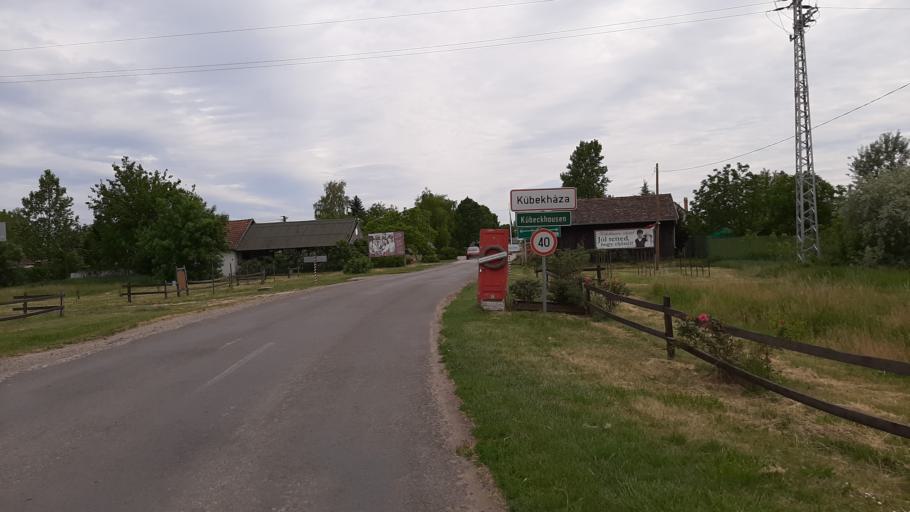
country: RO
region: Timis
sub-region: Comuna Beba Veche
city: Beba Veche
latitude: 46.1552
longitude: 20.2784
